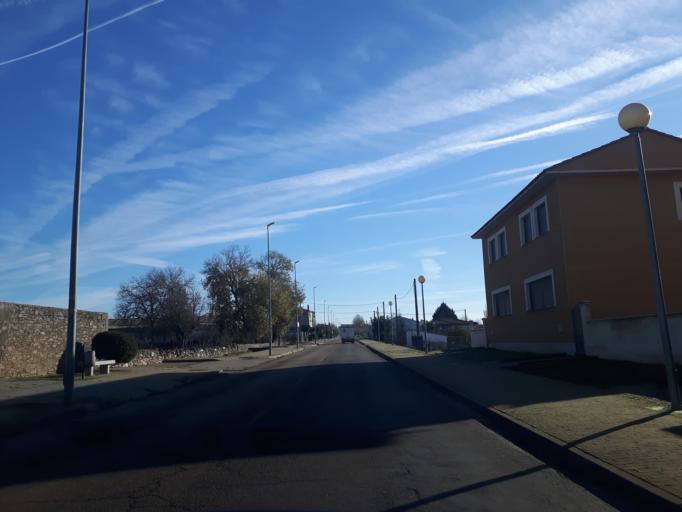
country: ES
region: Castille and Leon
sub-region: Provincia de Salamanca
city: Vitigudino
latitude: 41.0091
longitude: -6.4296
